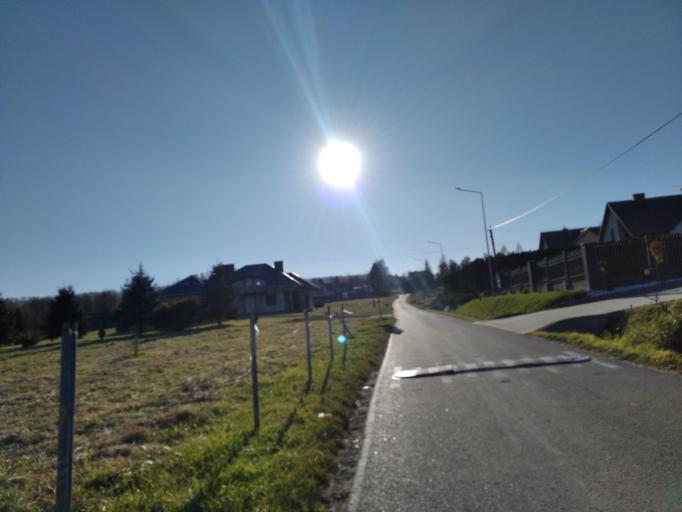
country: PL
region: Subcarpathian Voivodeship
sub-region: Powiat strzyzowski
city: Strzyzow
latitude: 49.8420
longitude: 21.8133
